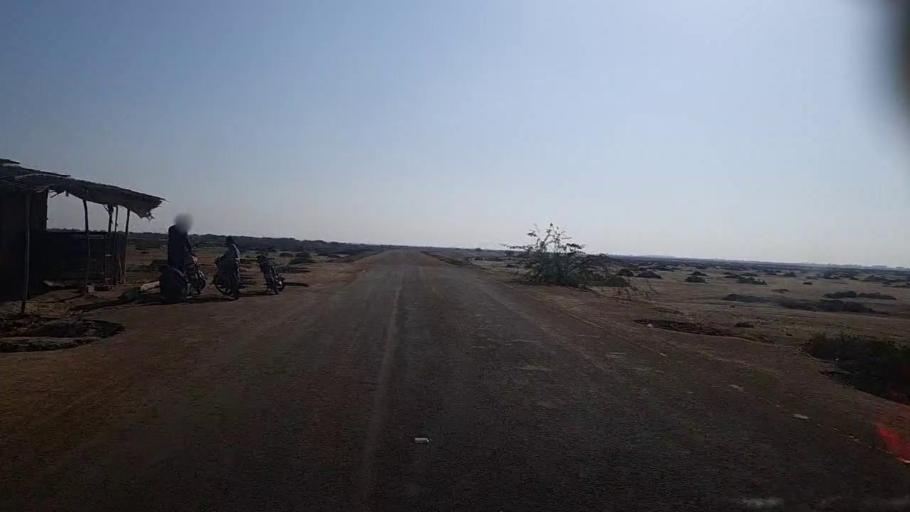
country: PK
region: Sindh
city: Mirpur Sakro
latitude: 24.5221
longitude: 67.4853
